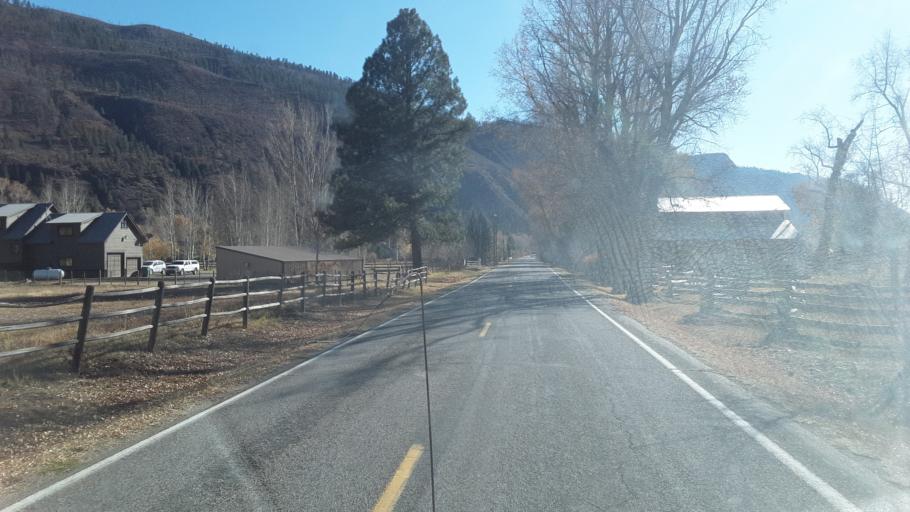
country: US
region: Colorado
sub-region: La Plata County
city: Durango
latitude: 37.4291
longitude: -107.7997
